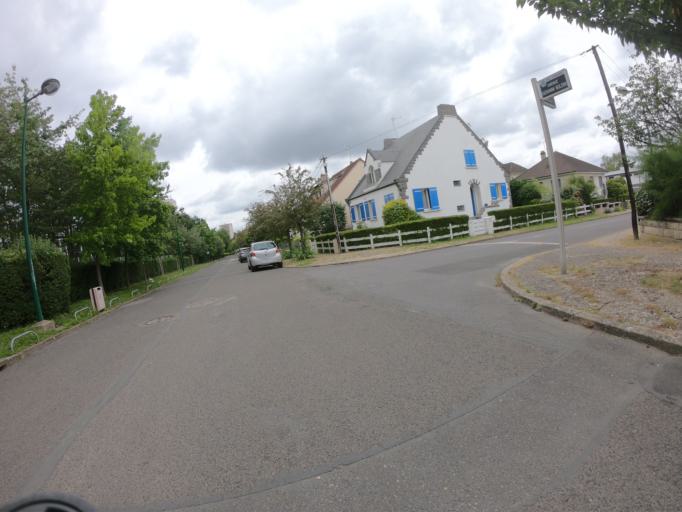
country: FR
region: Ile-de-France
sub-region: Departement des Hauts-de-Seine
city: Bourg-la-Reine
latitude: 48.7681
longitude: 2.3136
